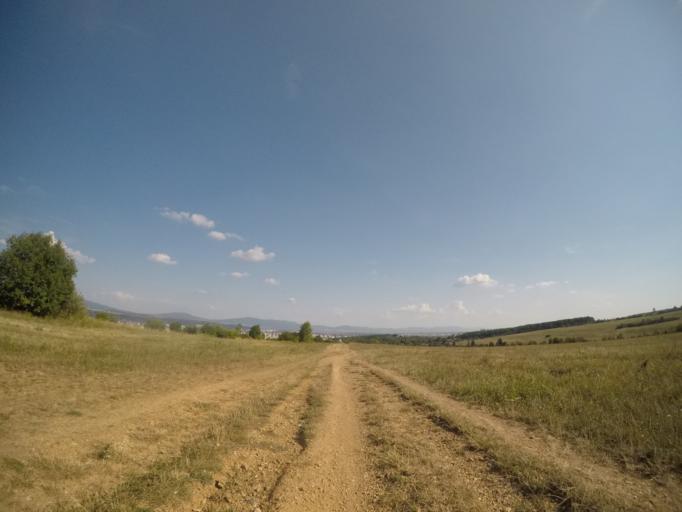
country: SK
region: Kosicky
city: Kosice
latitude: 48.7324
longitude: 21.2139
